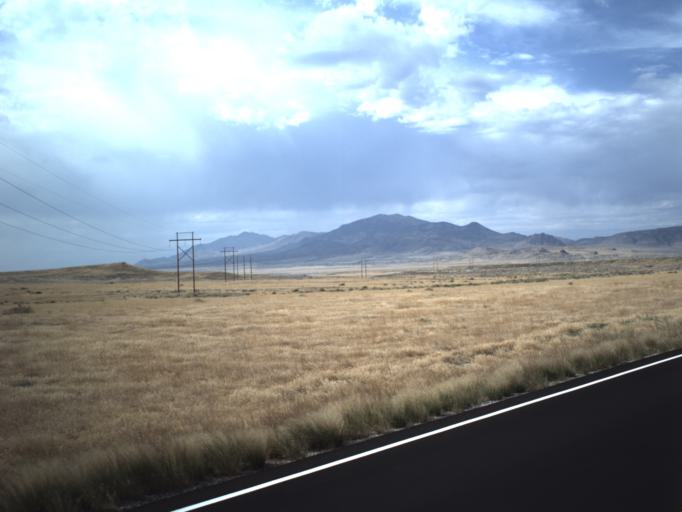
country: US
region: Utah
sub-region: Tooele County
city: Wendover
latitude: 41.4134
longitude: -113.9226
